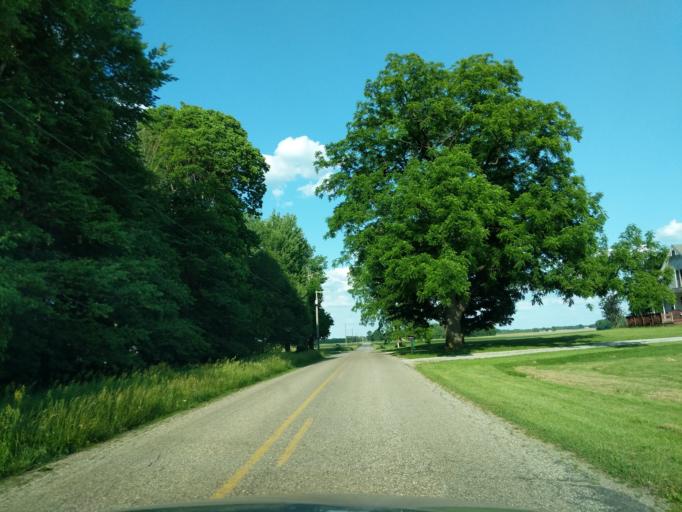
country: US
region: Indiana
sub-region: Kosciusko County
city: North Webster
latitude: 41.3024
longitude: -85.6214
